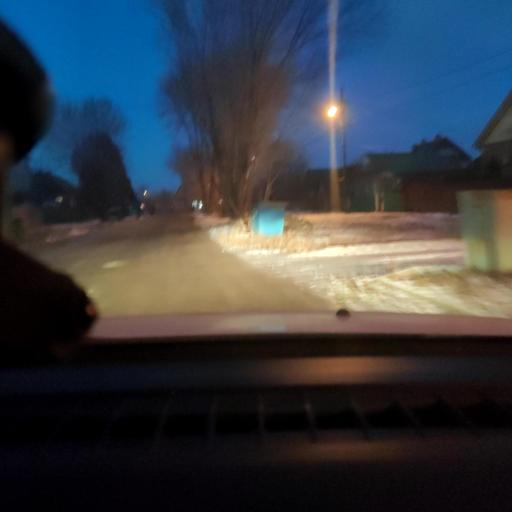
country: RU
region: Samara
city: Petra-Dubrava
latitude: 53.2556
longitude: 50.3389
